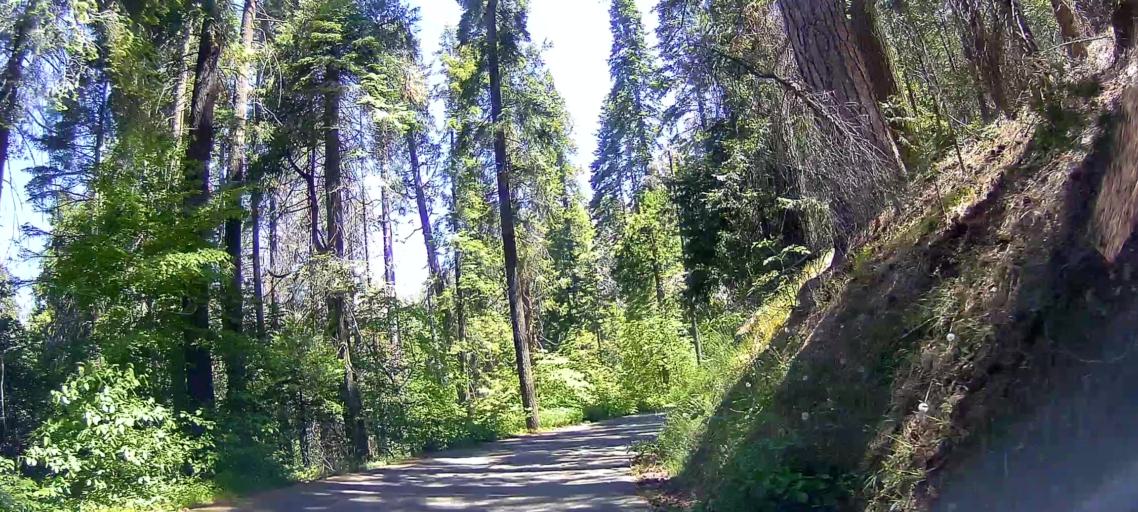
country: US
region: California
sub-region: Tulare County
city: Three Rivers
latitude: 36.5627
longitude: -118.7851
